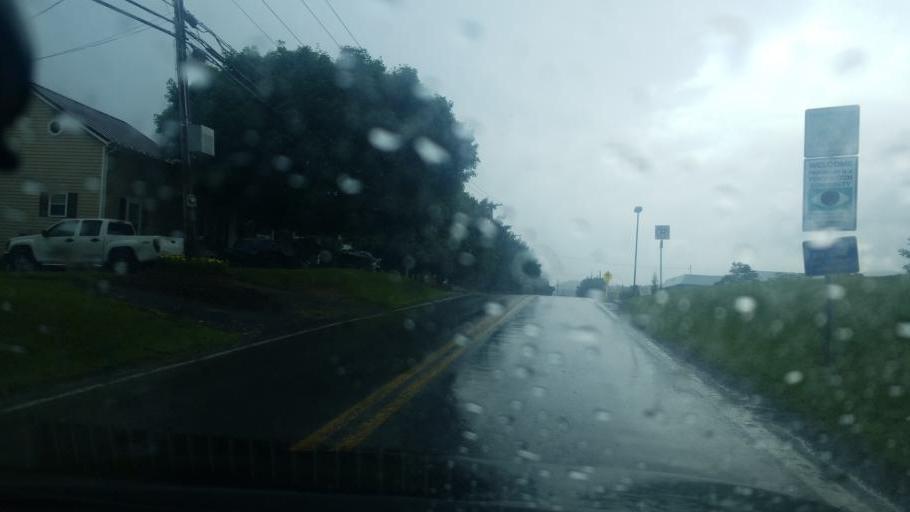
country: US
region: West Virginia
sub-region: Pendleton County
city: Franklin
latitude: 38.6520
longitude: -79.3250
